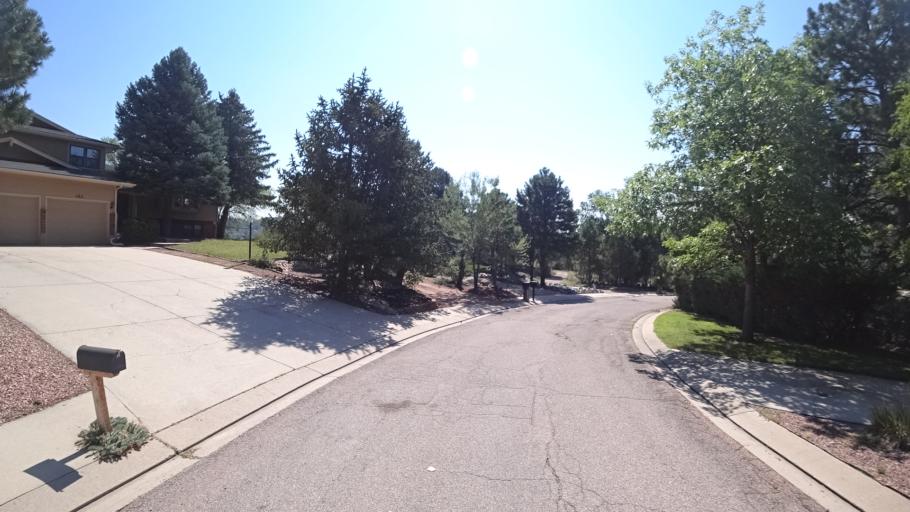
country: US
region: Colorado
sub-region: El Paso County
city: Air Force Academy
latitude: 38.9228
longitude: -104.8226
